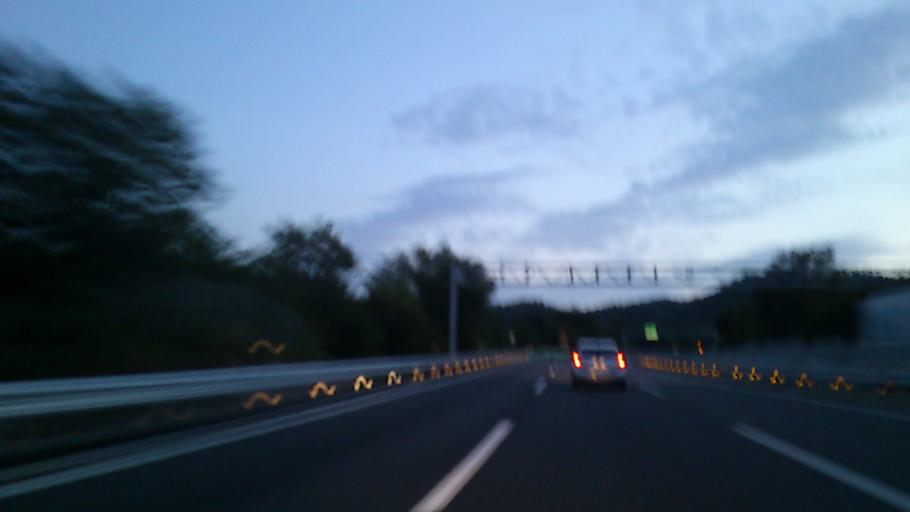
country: JP
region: Gifu
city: Tajimi
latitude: 35.3410
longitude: 137.0899
